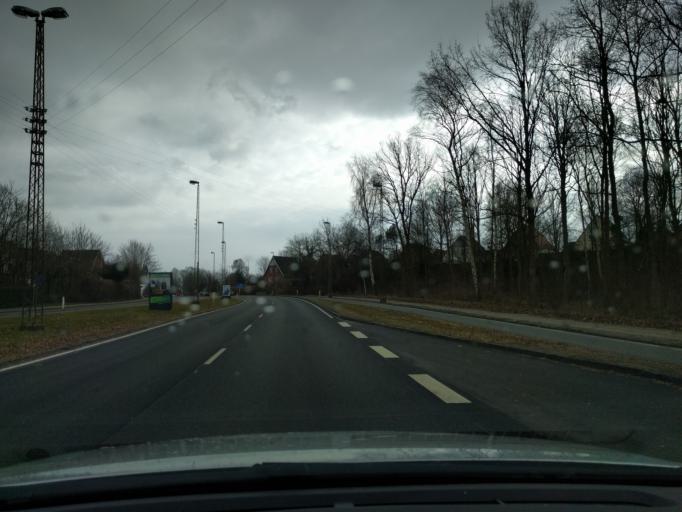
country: DK
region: South Denmark
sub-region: Odense Kommune
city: Odense
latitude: 55.3923
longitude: 10.3460
